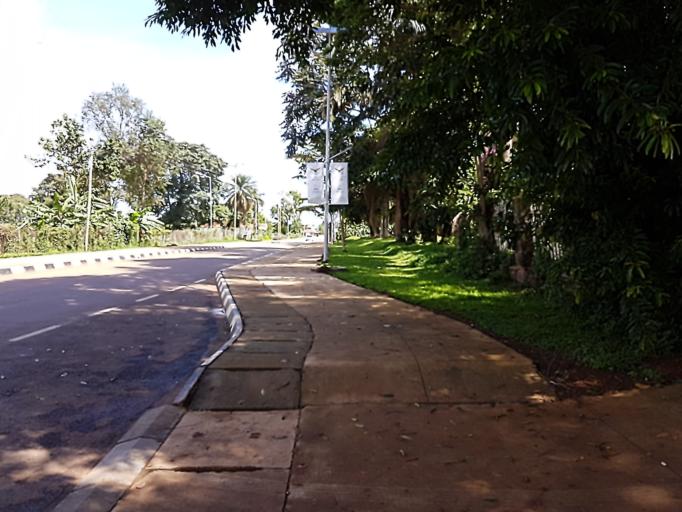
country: UG
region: Central Region
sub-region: Wakiso District
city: Entebbe
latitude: 0.0550
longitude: 32.4662
